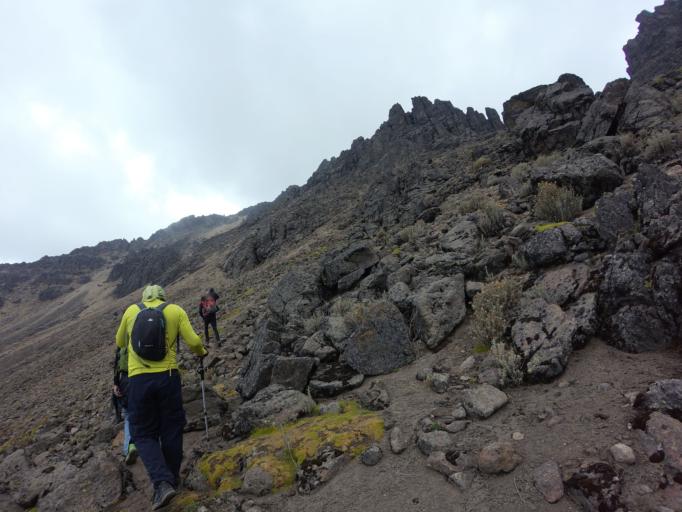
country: MX
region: Mexico
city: Amecameca de Juarez
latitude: 19.1495
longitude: -98.6379
